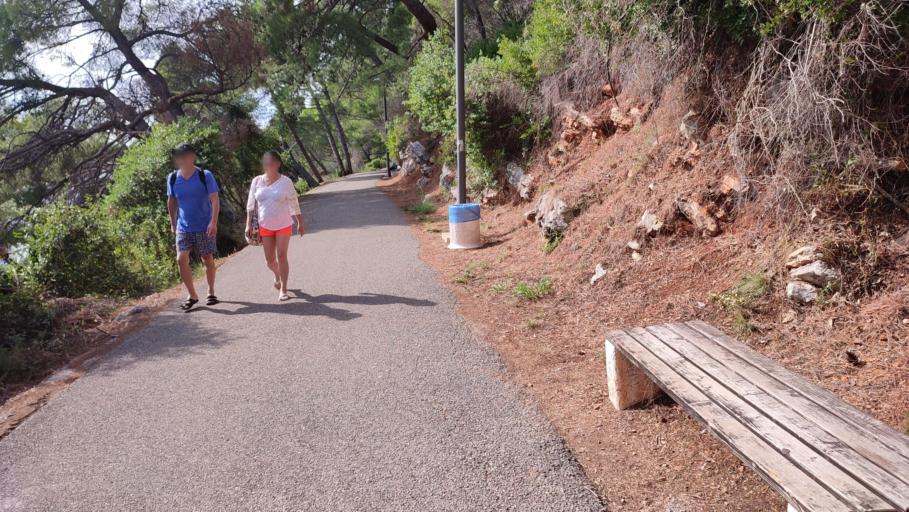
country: ME
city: Petrovac na Moru
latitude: 42.2064
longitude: 18.9338
